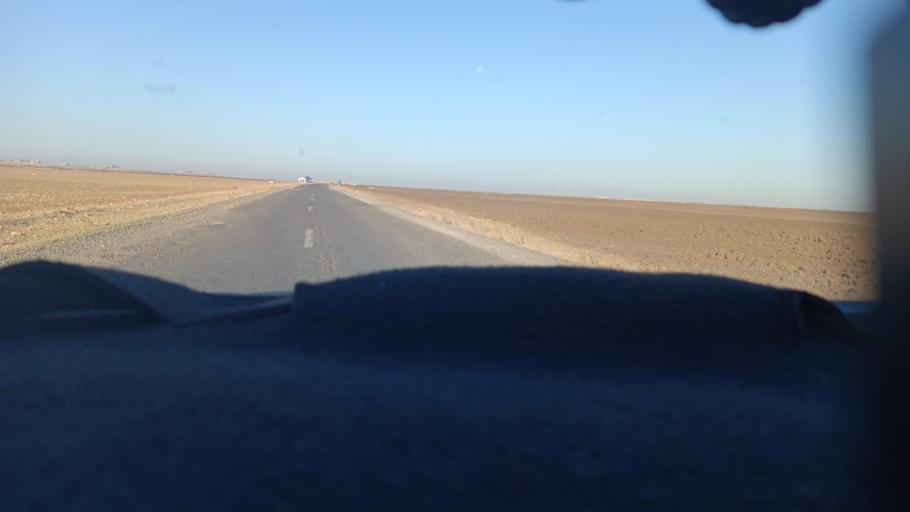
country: MA
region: Doukkala-Abda
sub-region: Safi
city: Youssoufia
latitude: 32.3723
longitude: -8.7017
